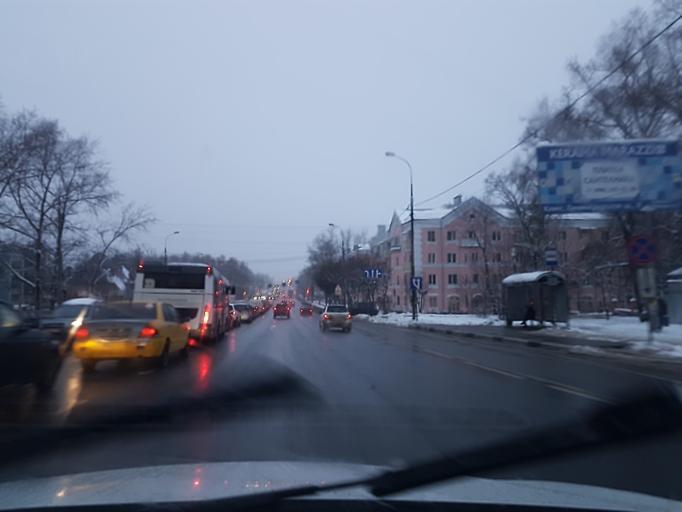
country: RU
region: Moskovskaya
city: Solnechnogorsk
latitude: 56.1897
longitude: 36.9743
